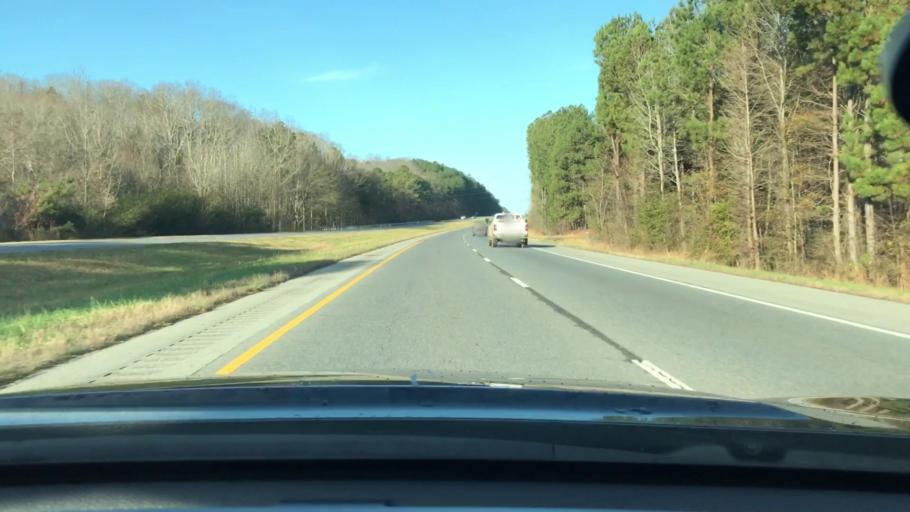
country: US
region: Alabama
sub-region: Shelby County
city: Harpersville
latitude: 33.3521
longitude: -86.4764
